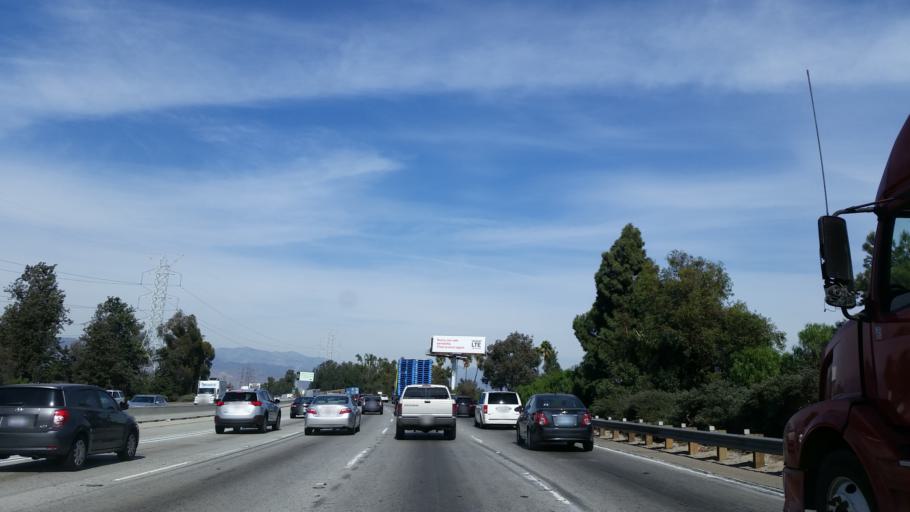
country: US
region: California
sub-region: Los Angeles County
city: Avocado Heights
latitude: 34.0429
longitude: -118.0111
